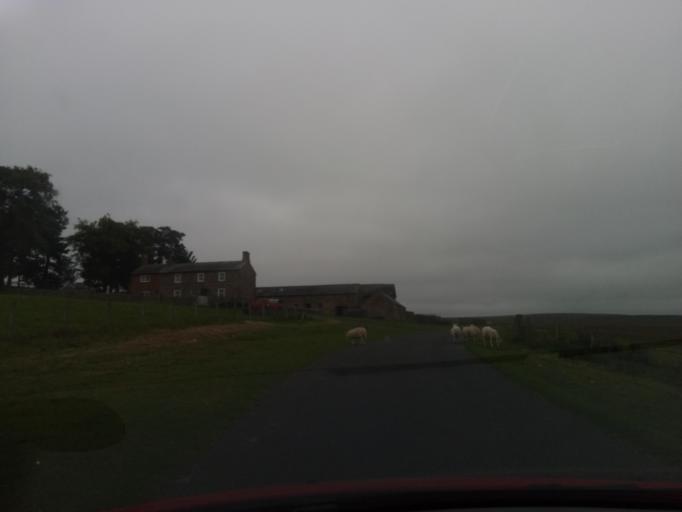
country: GB
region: England
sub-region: Northumberland
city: Rochester
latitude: 55.2944
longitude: -2.2072
